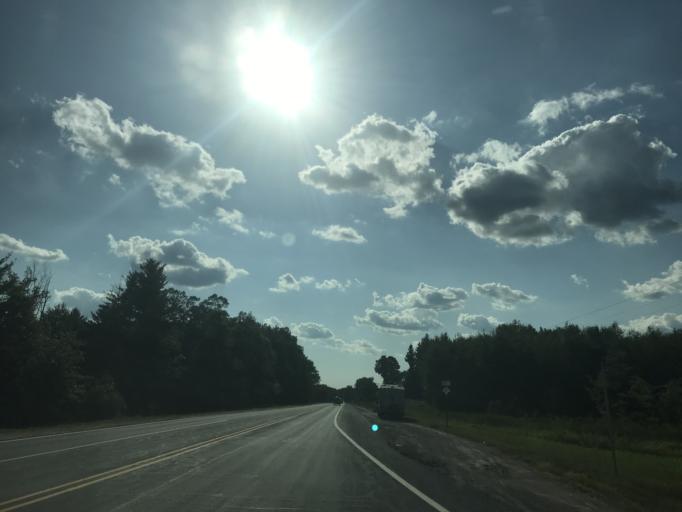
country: US
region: Michigan
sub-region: Newaygo County
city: White Cloud
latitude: 43.5687
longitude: -85.7718
